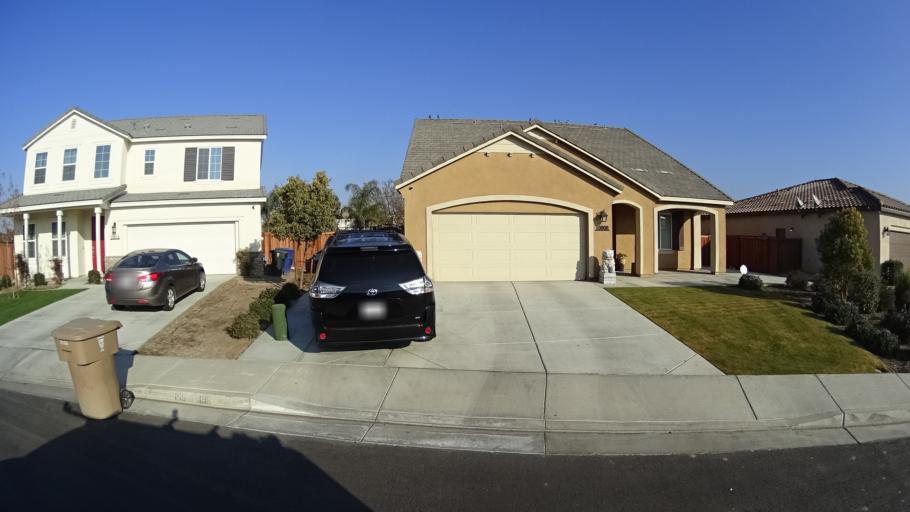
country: US
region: California
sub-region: Kern County
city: Greenacres
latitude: 35.3028
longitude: -119.1139
